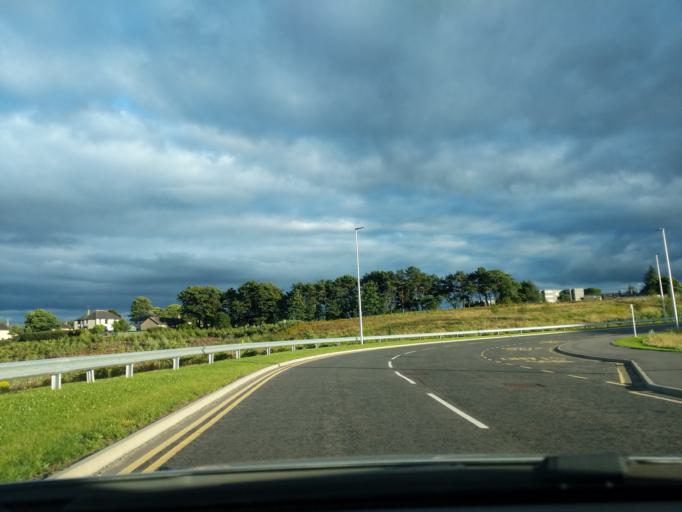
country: GB
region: Scotland
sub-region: Aberdeen City
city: Dyce
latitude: 57.1846
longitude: -2.1868
